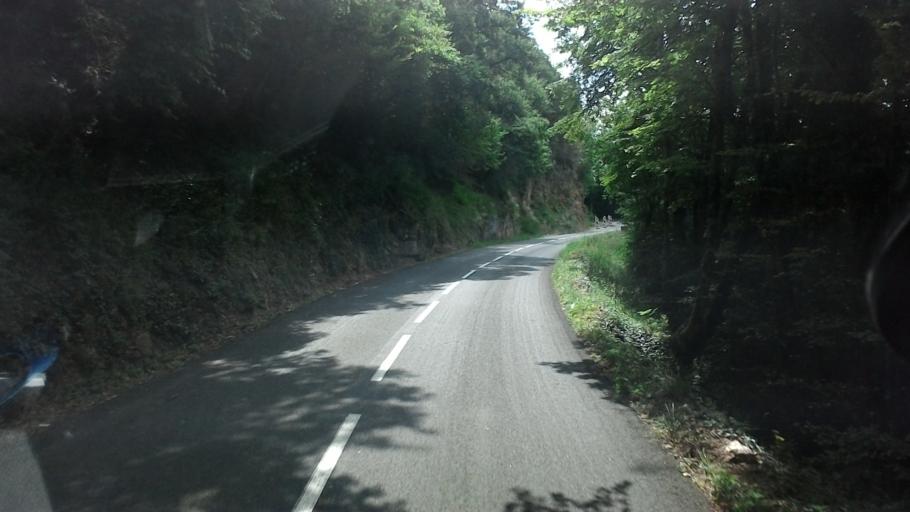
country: FR
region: Rhone-Alpes
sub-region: Departement de l'Ain
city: Saint-Sorlin-en-Bugey
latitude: 45.8841
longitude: 5.3790
